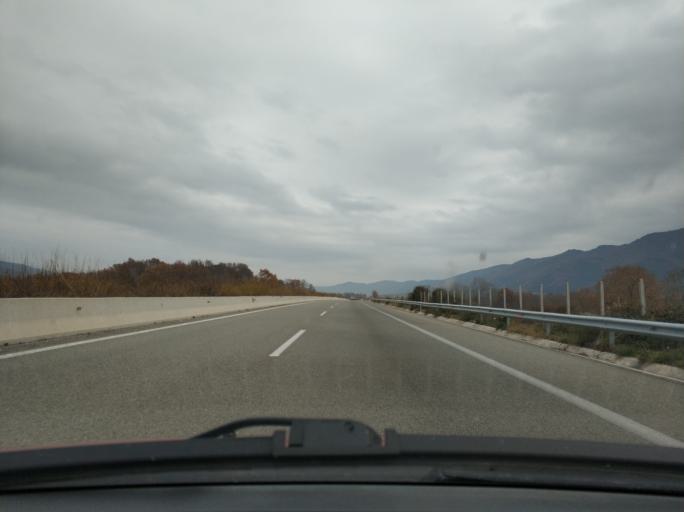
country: GR
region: East Macedonia and Thrace
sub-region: Nomos Kavalas
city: Palaiochori
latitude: 40.8603
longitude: 24.1679
